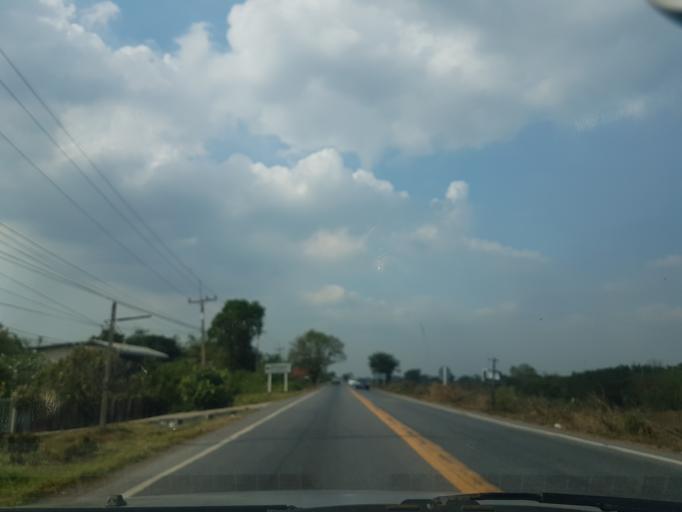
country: TH
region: Phra Nakhon Si Ayutthaya
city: Phachi
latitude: 14.4694
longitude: 100.7488
